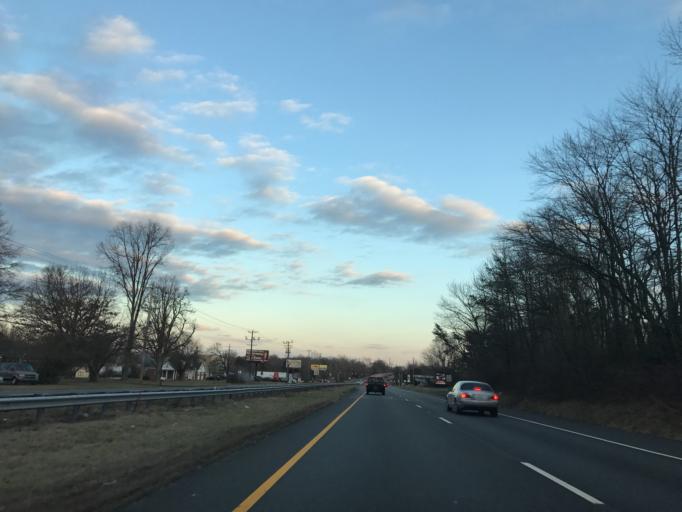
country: US
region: Maryland
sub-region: Cecil County
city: Elkton
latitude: 39.6071
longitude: -75.8580
